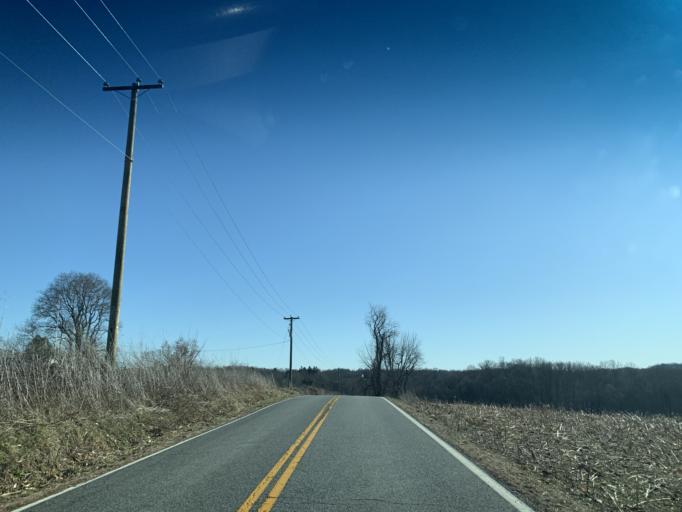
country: US
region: Maryland
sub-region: Cecil County
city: Rising Sun
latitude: 39.6626
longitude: -76.1031
